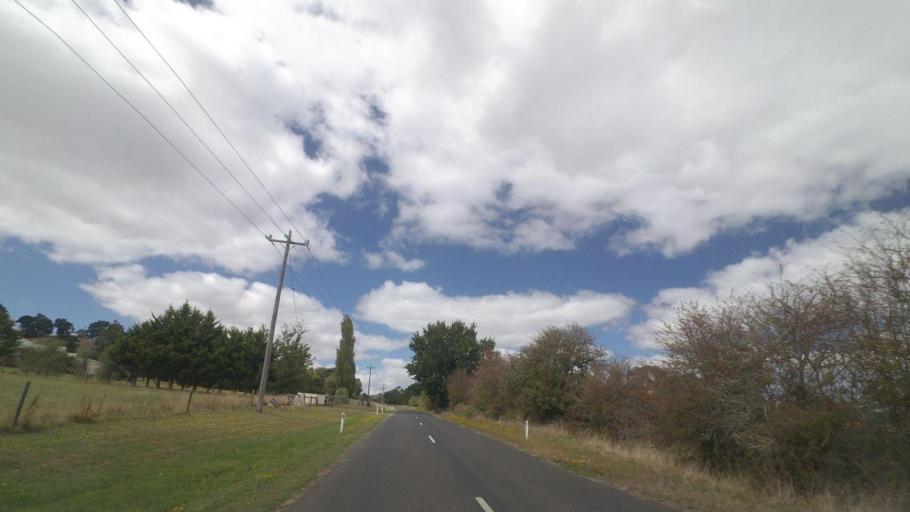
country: AU
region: Victoria
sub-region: Cardinia
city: Bunyip
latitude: -38.3506
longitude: 145.7003
